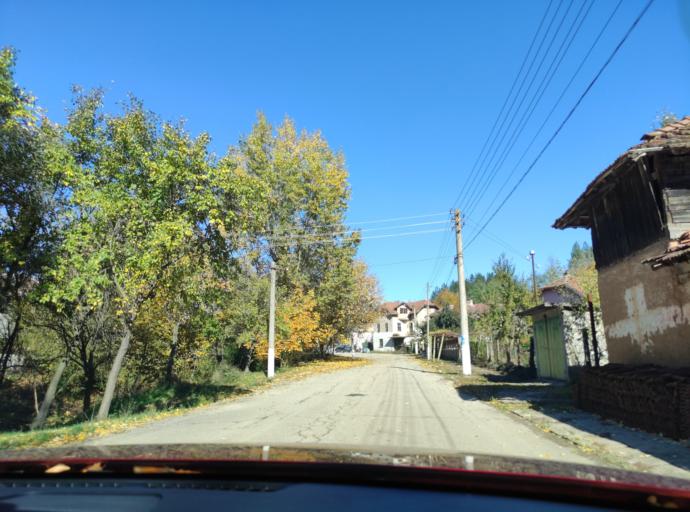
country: BG
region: Montana
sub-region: Obshtina Montana
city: Montana
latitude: 43.4174
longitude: 23.0670
